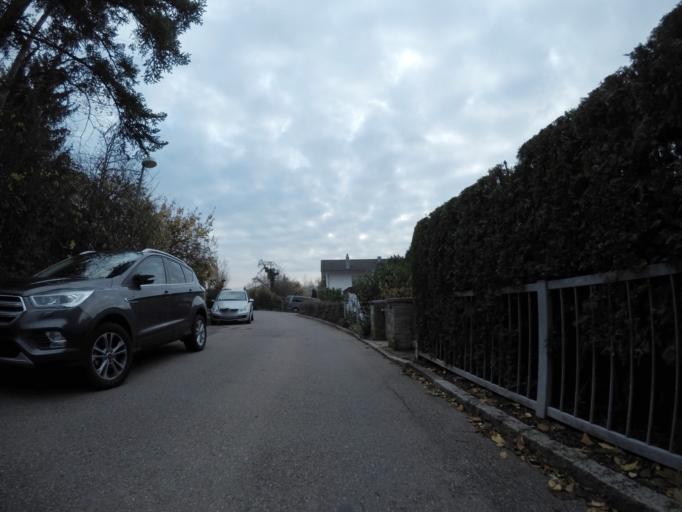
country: DE
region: Baden-Wuerttemberg
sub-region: Tuebingen Region
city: Reutlingen
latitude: 48.5021
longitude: 9.2277
